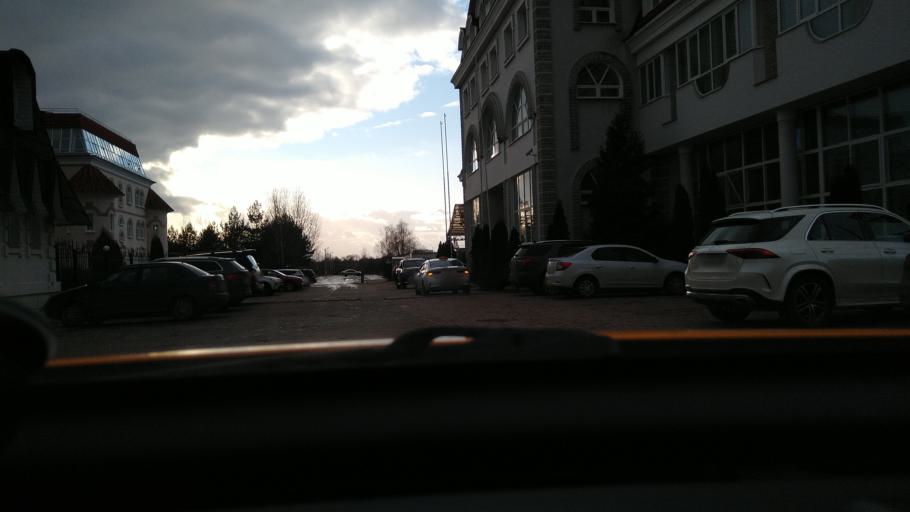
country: RU
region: Moskovskaya
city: Petrovo-Dal'neye
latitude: 55.7499
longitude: 37.1884
